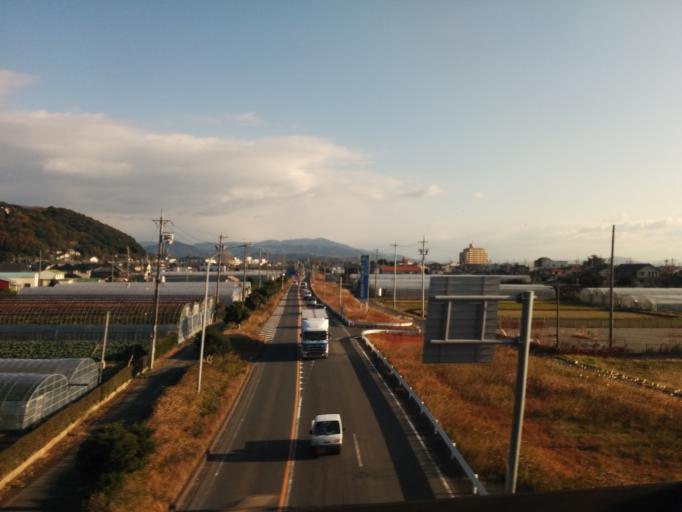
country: JP
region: Aichi
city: Kozakai-cho
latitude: 34.8090
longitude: 137.3073
